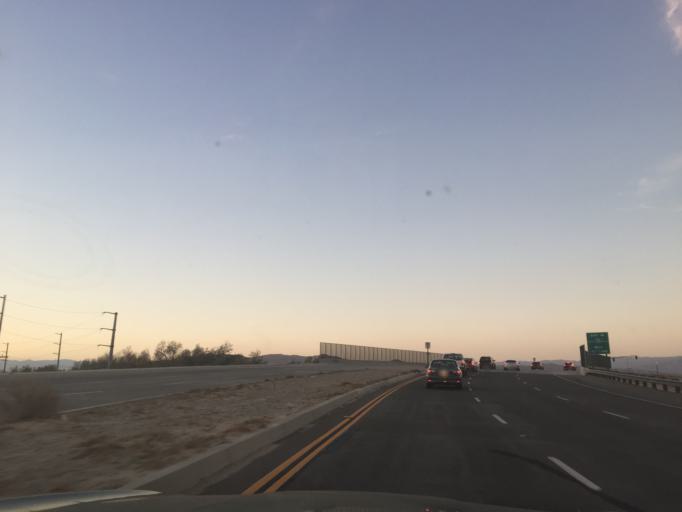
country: US
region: California
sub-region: Riverside County
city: Thousand Palms
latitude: 33.8172
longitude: -116.4105
